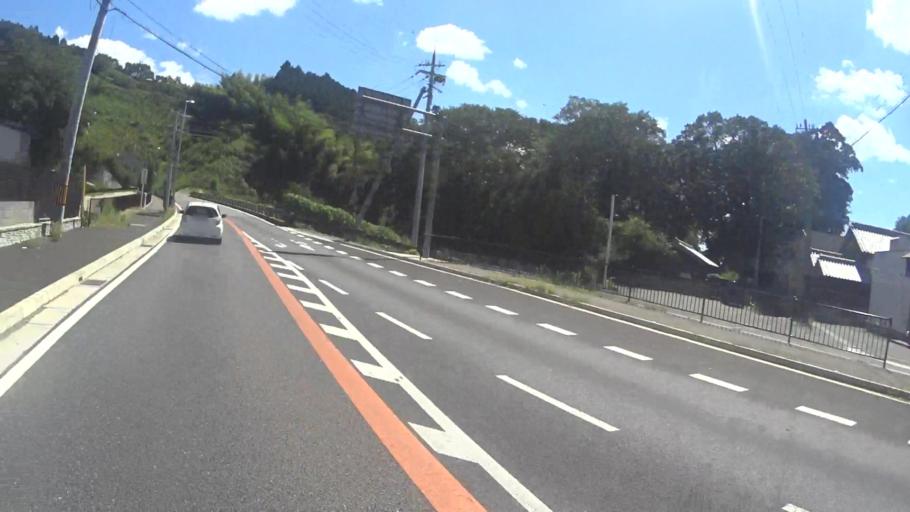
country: JP
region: Nara
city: Nara-shi
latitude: 34.7682
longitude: 135.8773
